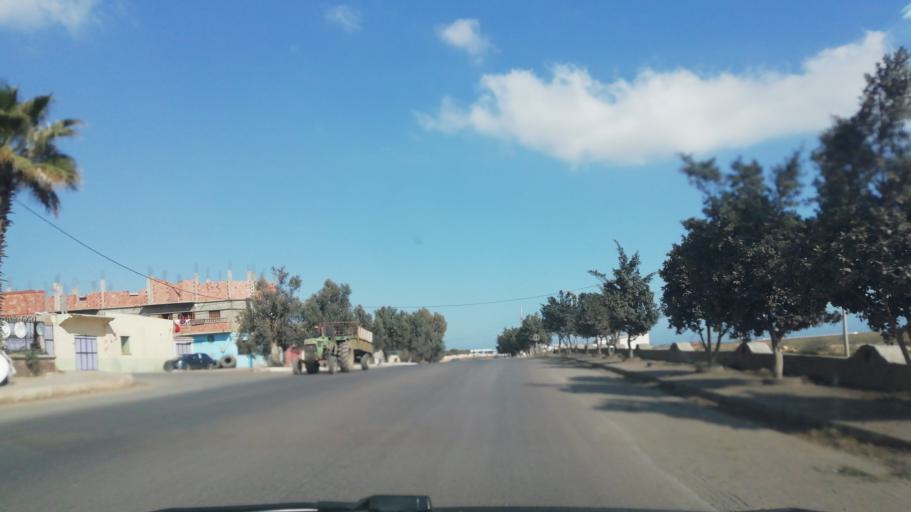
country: DZ
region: Oran
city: Ain el Bya
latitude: 35.7763
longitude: -0.2791
